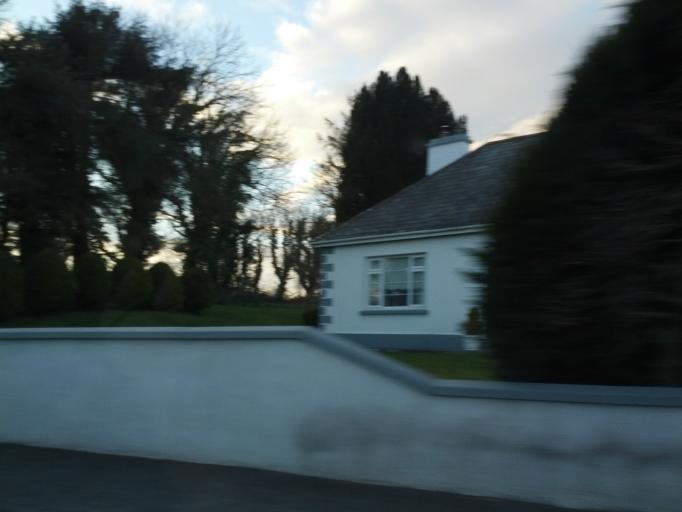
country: IE
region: Connaught
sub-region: County Galway
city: Athenry
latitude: 53.3154
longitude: -8.6167
